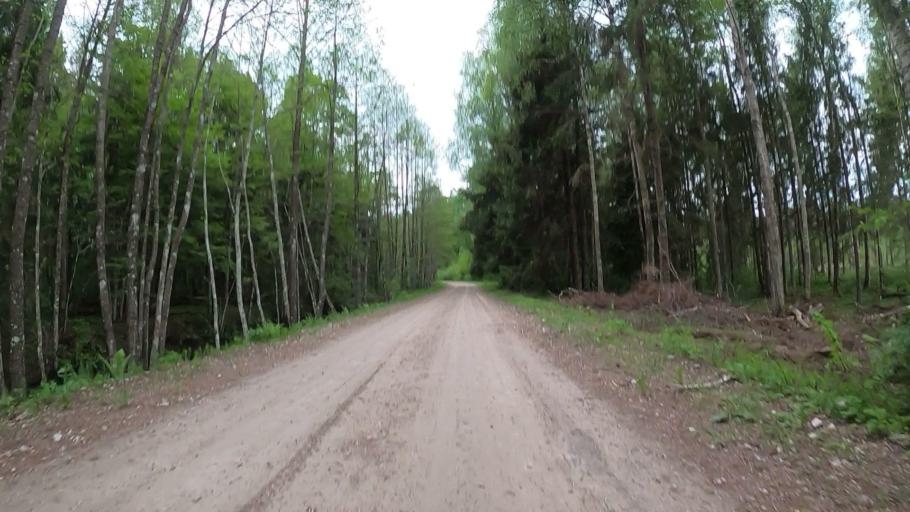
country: LV
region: Ozolnieku
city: Ozolnieki
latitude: 56.7940
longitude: 23.7779
